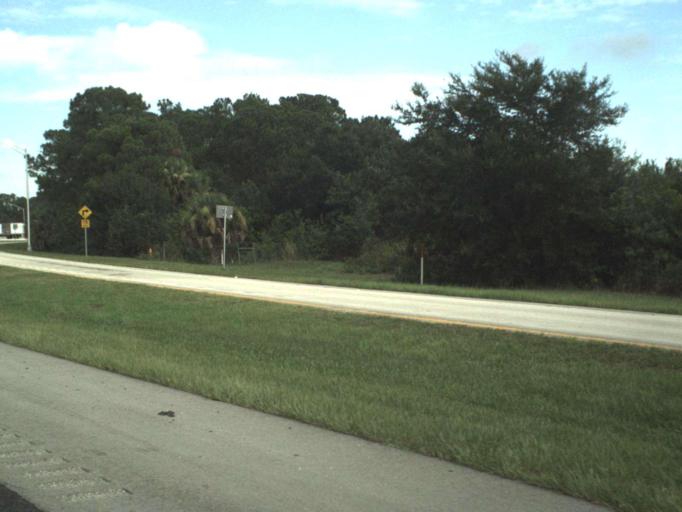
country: US
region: Florida
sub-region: Saint Lucie County
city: Lakewood Park
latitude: 27.4638
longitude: -80.4157
